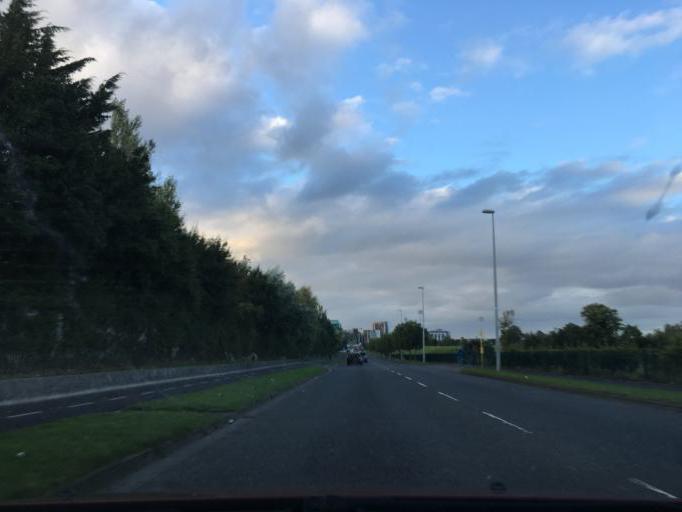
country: IE
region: Leinster
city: Oldbawn
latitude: 53.2779
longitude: -6.3739
